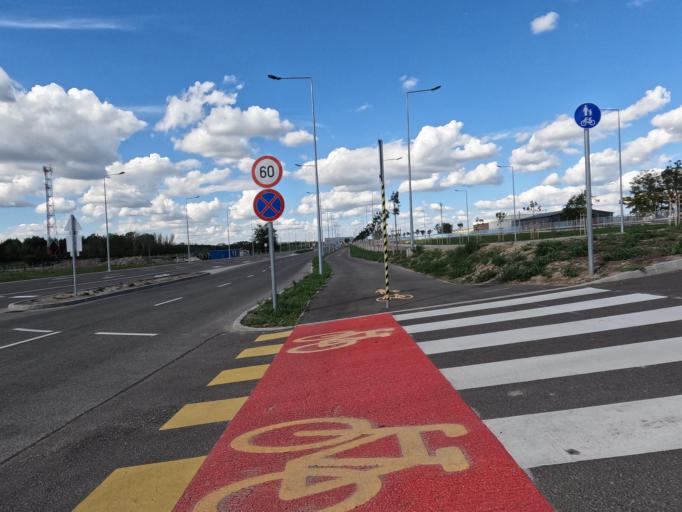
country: HU
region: Tolna
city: Paks
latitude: 46.5777
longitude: 18.8459
